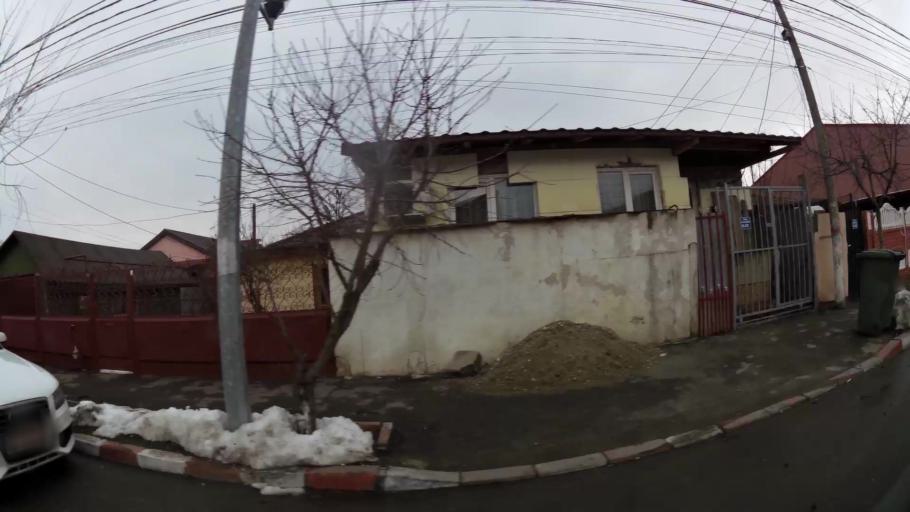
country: RO
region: Ilfov
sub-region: Voluntari City
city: Voluntari
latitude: 44.4804
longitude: 26.1818
